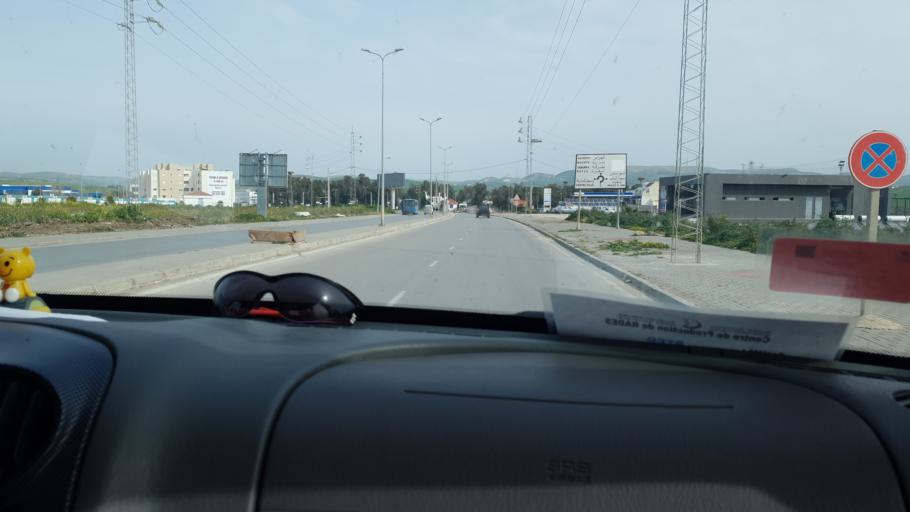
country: TN
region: Bajah
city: Beja
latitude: 36.7279
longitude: 9.2062
